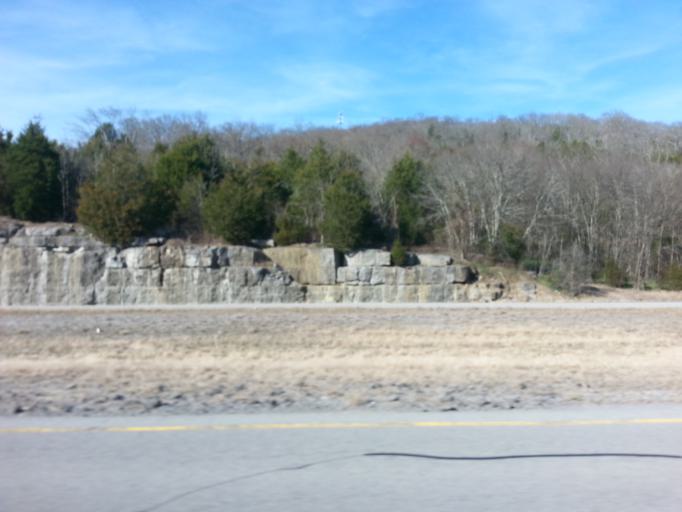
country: US
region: Tennessee
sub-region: Cannon County
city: Woodbury
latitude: 35.8093
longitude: -86.2066
